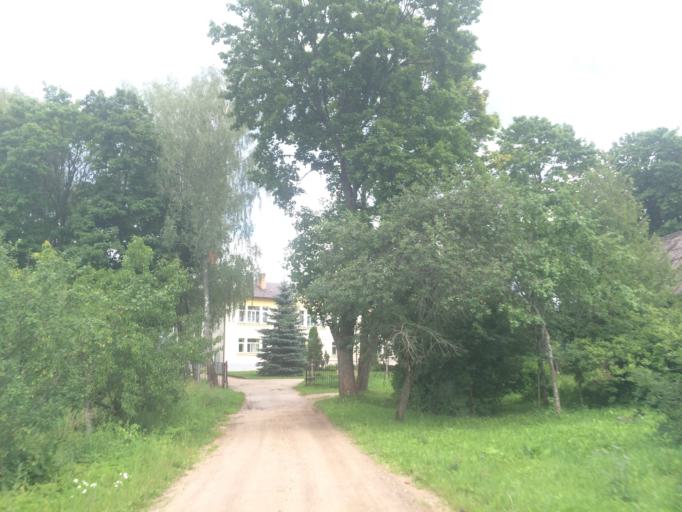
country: LV
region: Rezekne
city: Rezekne
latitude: 56.6623
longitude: 27.2753
